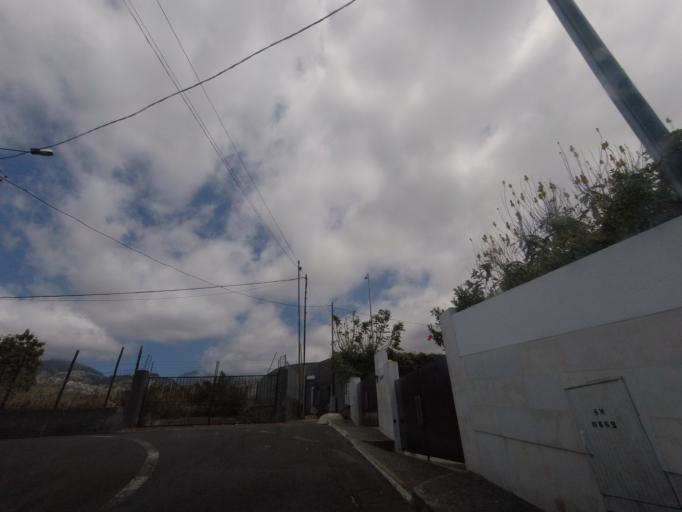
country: PT
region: Madeira
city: Camara de Lobos
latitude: 32.6468
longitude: -16.9635
